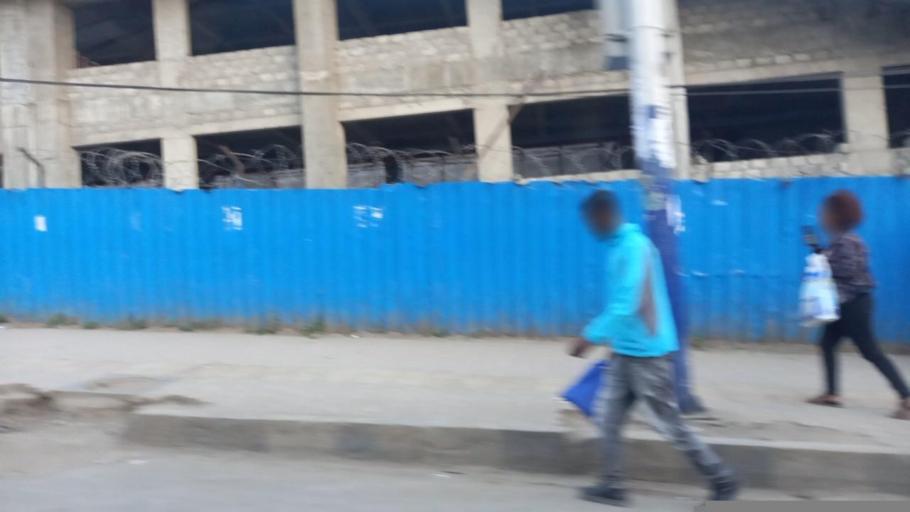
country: ET
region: Adis Abeba
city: Addis Ababa
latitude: 9.0344
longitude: 38.7518
